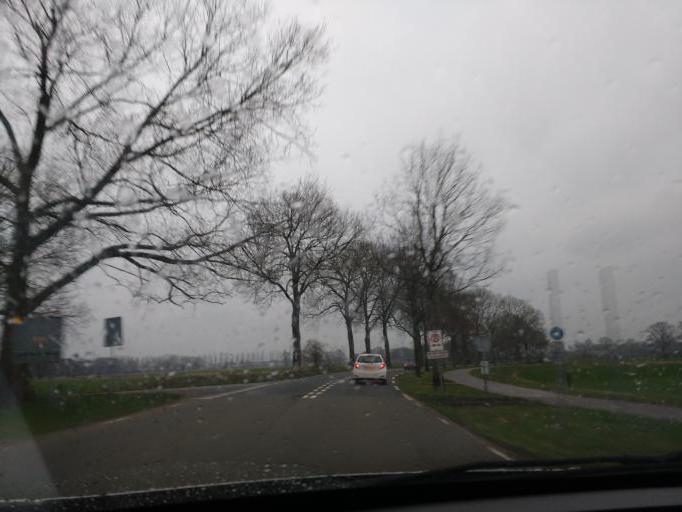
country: NL
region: North Brabant
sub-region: Gemeente Boxmeer
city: Overloon
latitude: 51.5584
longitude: 5.9589
